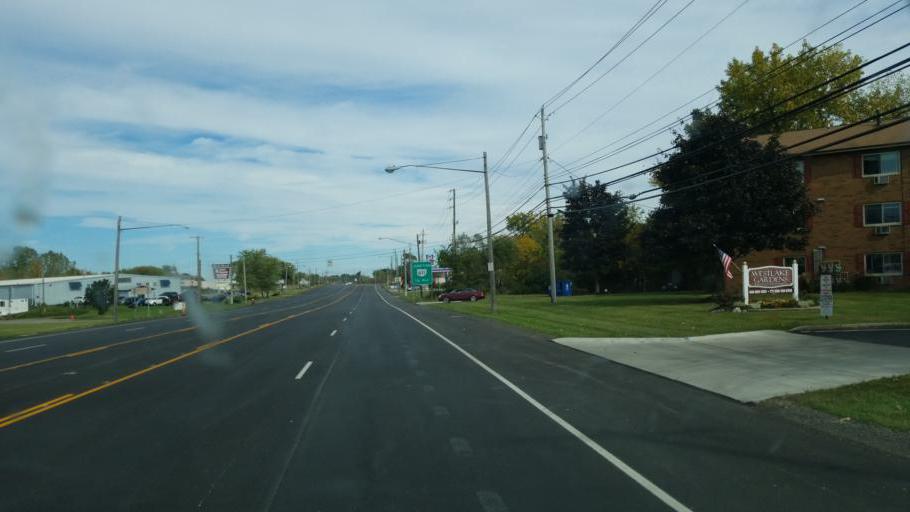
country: US
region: Ohio
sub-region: Lorain County
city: Amherst
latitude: 41.4426
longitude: -82.2321
